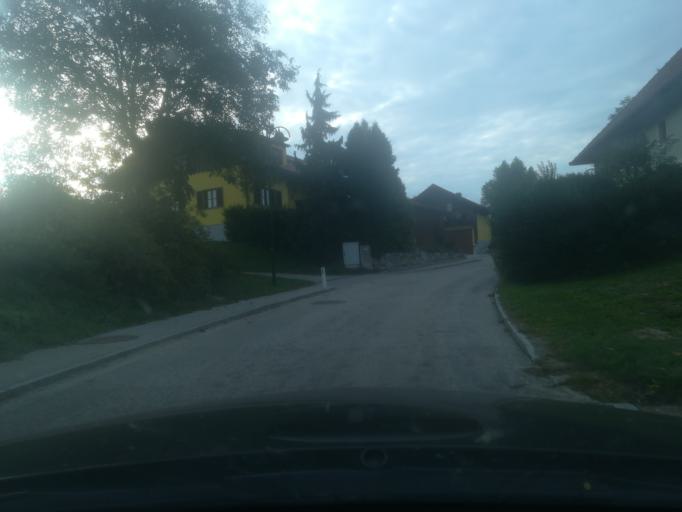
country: AT
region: Upper Austria
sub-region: Wels-Land
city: Buchkirchen
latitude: 48.2576
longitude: 14.0423
